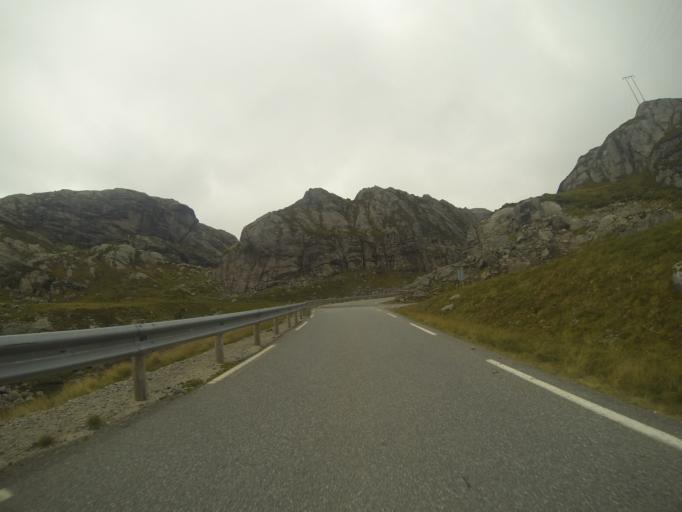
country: NO
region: Vest-Agder
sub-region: Sirdal
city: Tonstad
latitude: 59.0321
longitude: 6.6553
